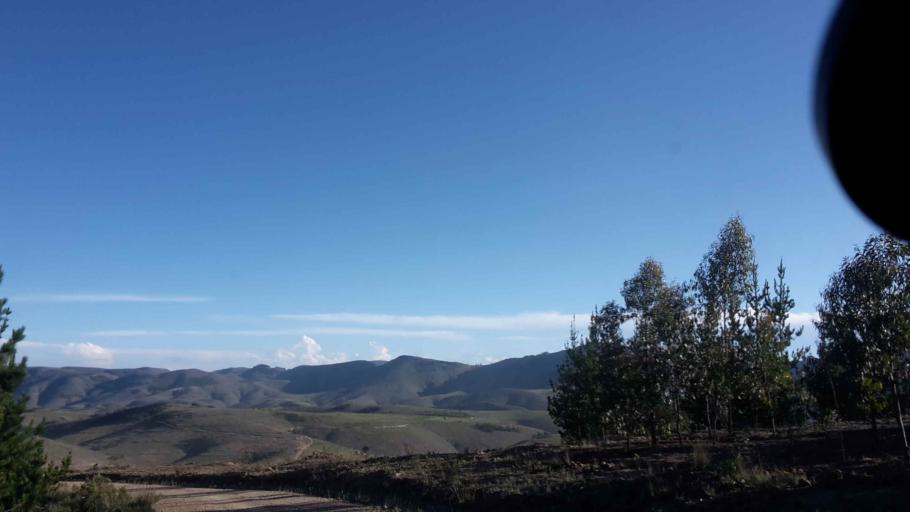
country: BO
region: Cochabamba
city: Arani
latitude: -17.7409
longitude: -65.6245
